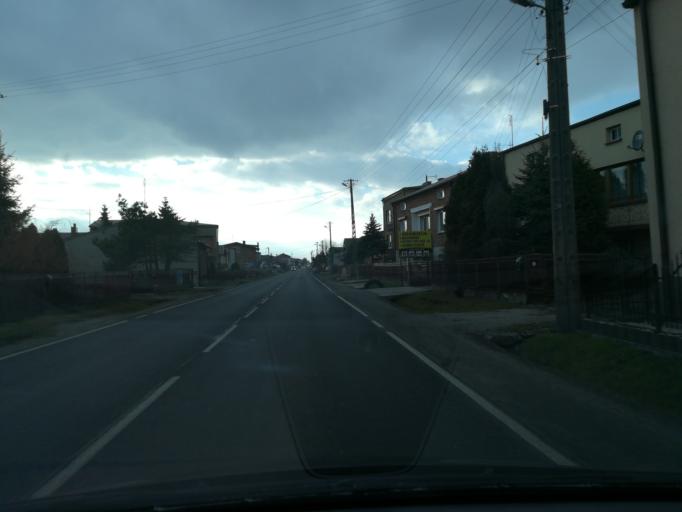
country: PL
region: Lodz Voivodeship
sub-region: Powiat radomszczanski
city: Radomsko
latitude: 51.0774
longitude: 19.3937
